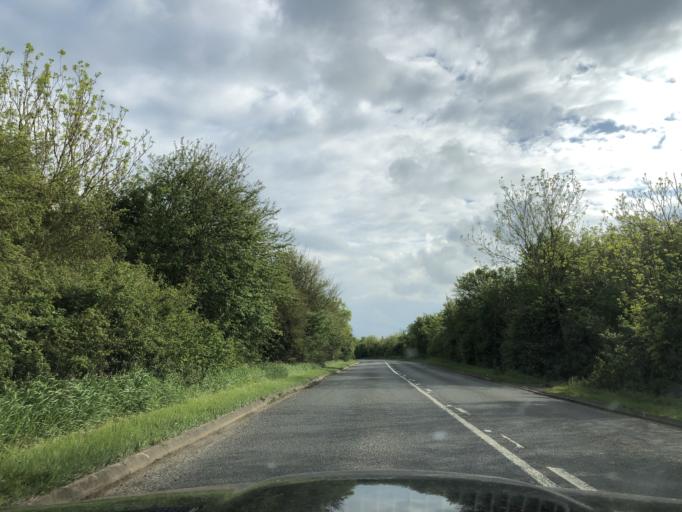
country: GB
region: England
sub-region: Warwickshire
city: Shipston on Stour
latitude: 52.0533
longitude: -1.6634
